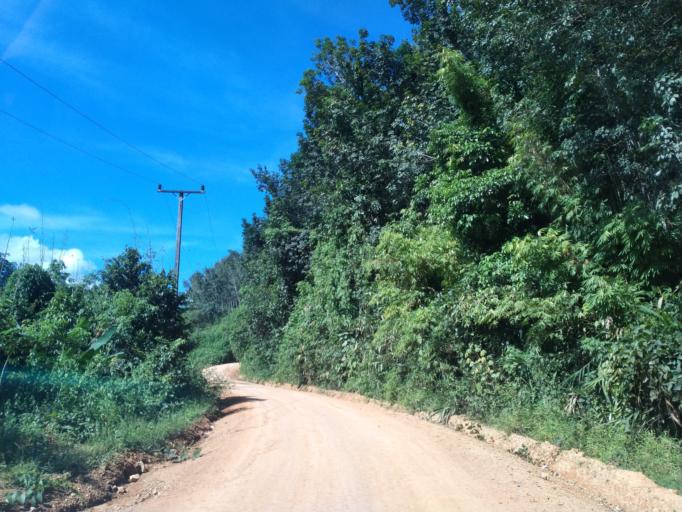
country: TH
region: Changwat Bueng Kan
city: Pak Khat
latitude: 18.6317
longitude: 103.0691
